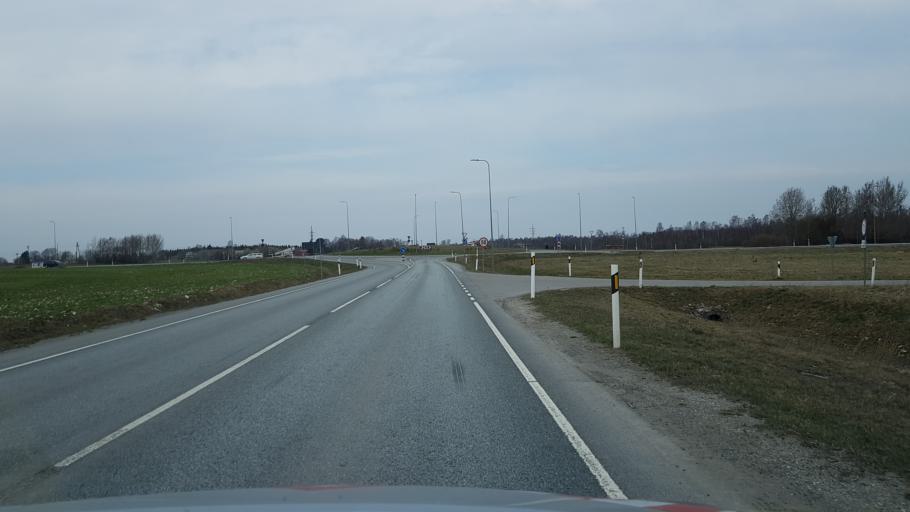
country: EE
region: Laeaene-Virumaa
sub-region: Someru vald
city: Someru
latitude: 59.3545
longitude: 26.3971
